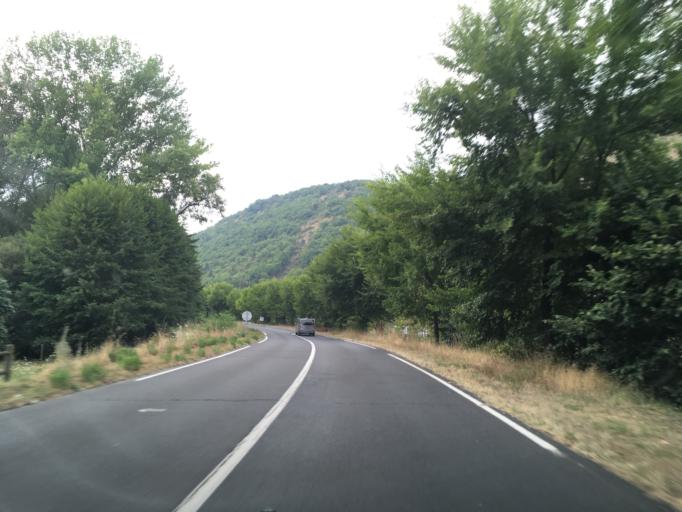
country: FR
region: Midi-Pyrenees
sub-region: Departement du Lot
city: Souillac
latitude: 44.8883
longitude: 1.4041
